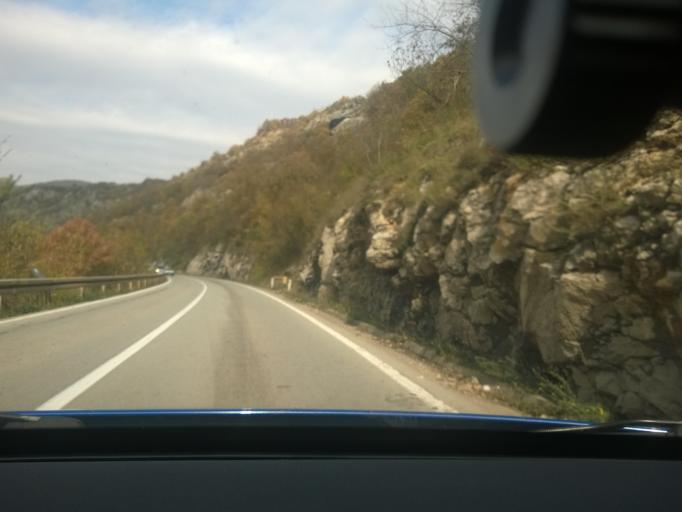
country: RS
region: Central Serbia
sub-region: Nisavski Okrug
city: Svrljig
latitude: 43.3299
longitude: 22.0994
